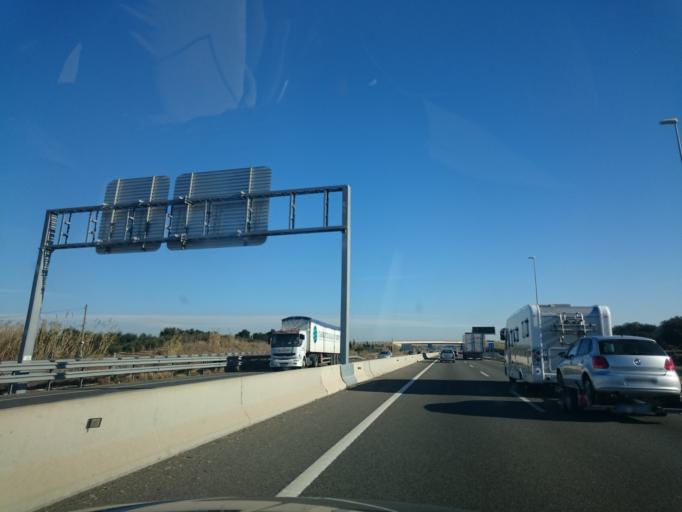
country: ES
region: Catalonia
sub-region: Provincia de Tarragona
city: Salou
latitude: 41.0942
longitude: 1.1055
